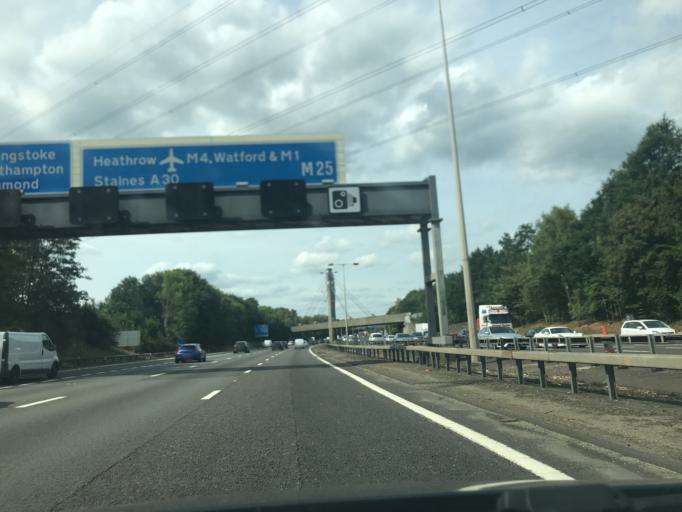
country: GB
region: England
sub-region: Surrey
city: Chertsey
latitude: 51.3908
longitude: -0.5300
